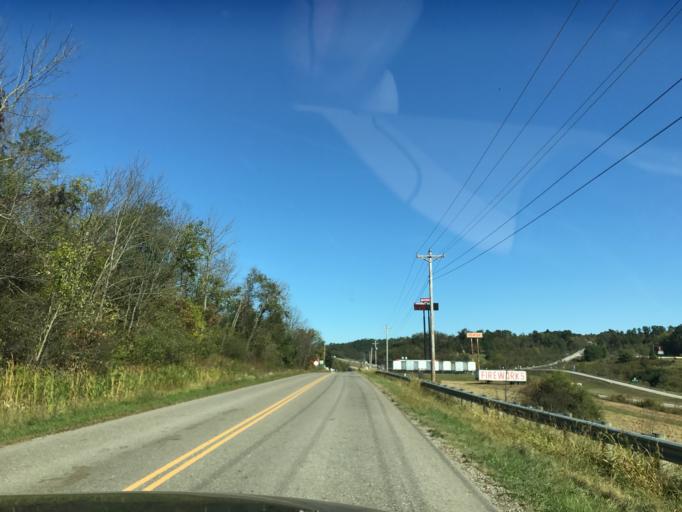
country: US
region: Ohio
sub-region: Belmont County
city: Barnesville
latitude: 40.0520
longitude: -81.3310
